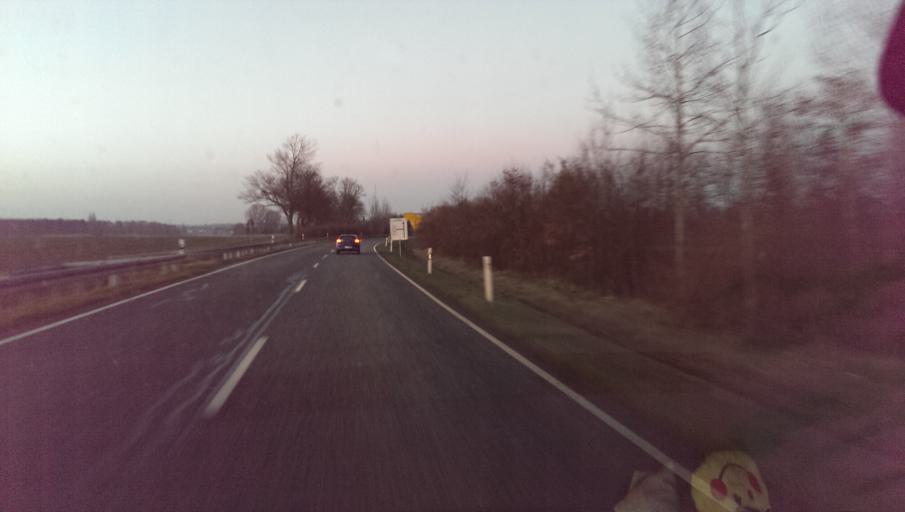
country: DE
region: Brandenburg
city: Juterbog
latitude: 51.9738
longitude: 13.1041
